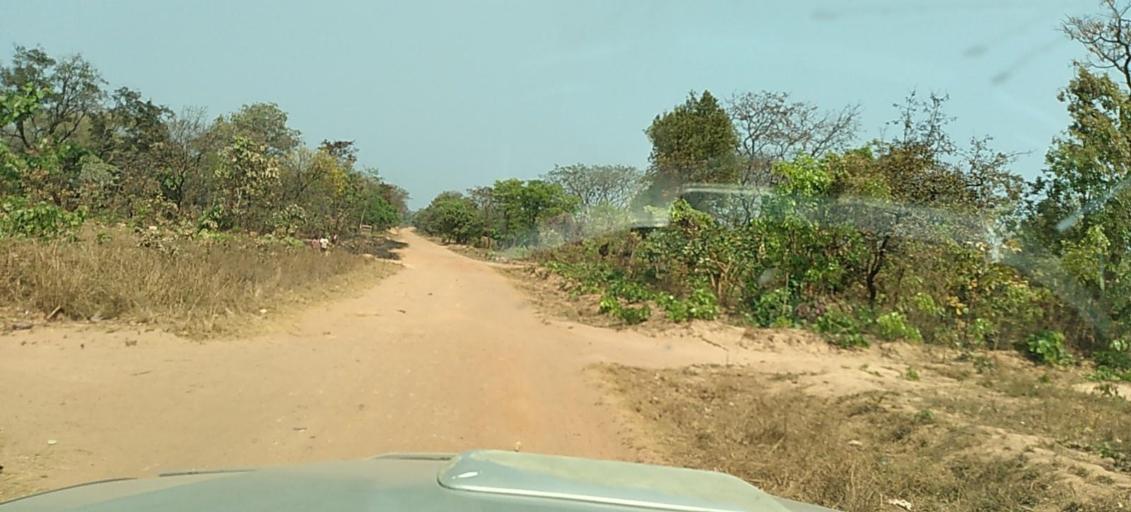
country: ZM
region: North-Western
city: Kasempa
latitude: -13.6955
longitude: 26.3266
